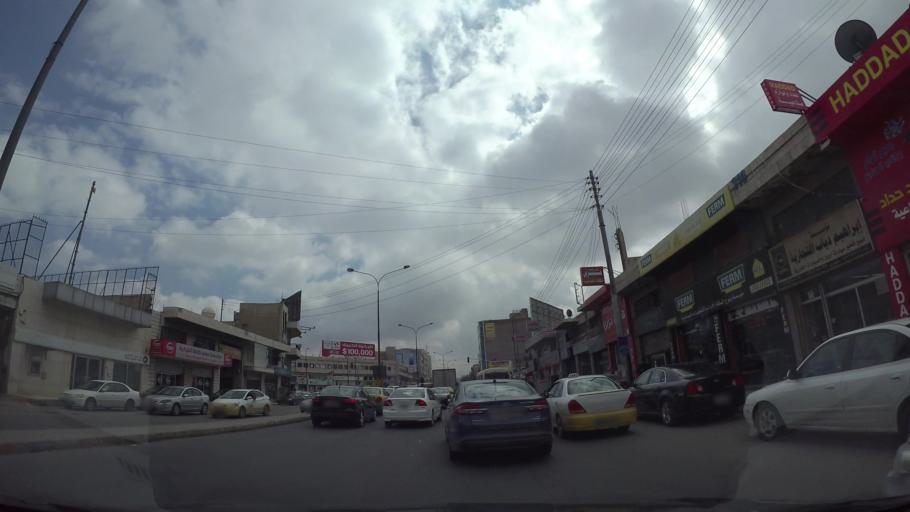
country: JO
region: Amman
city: Al Quwaysimah
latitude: 31.9221
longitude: 35.9381
